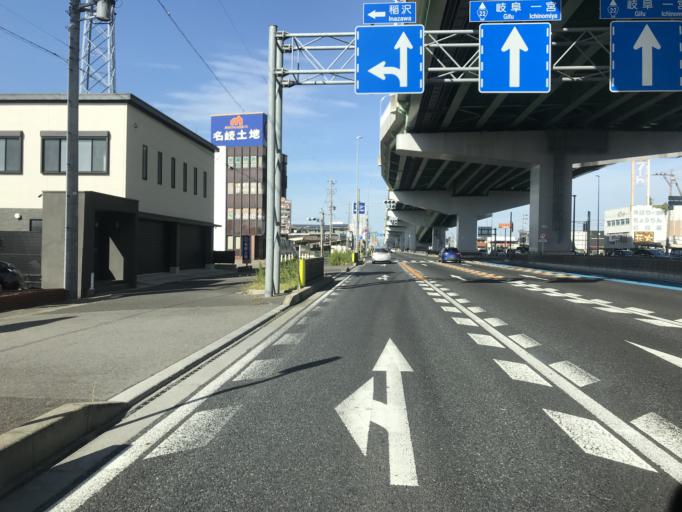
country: JP
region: Aichi
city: Iwakura
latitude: 35.2463
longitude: 136.8450
